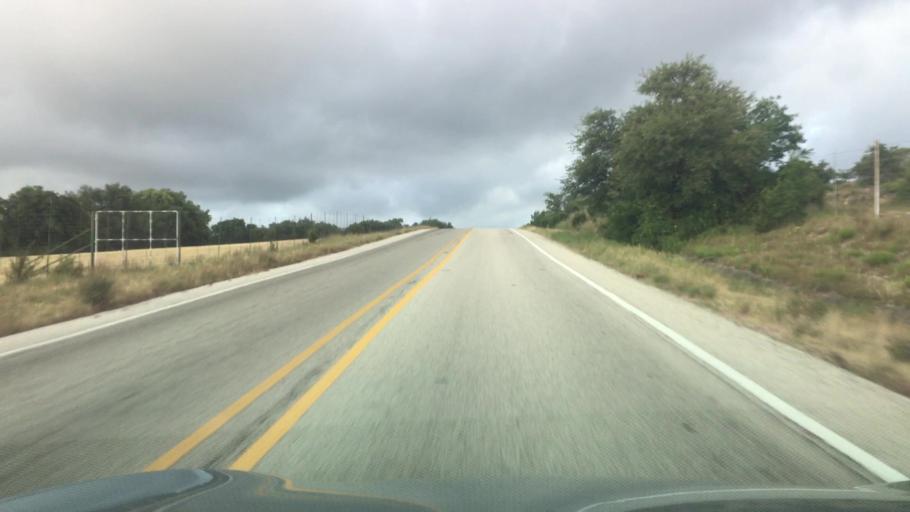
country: US
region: Texas
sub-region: Hays County
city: Dripping Springs
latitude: 30.1526
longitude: -98.2539
